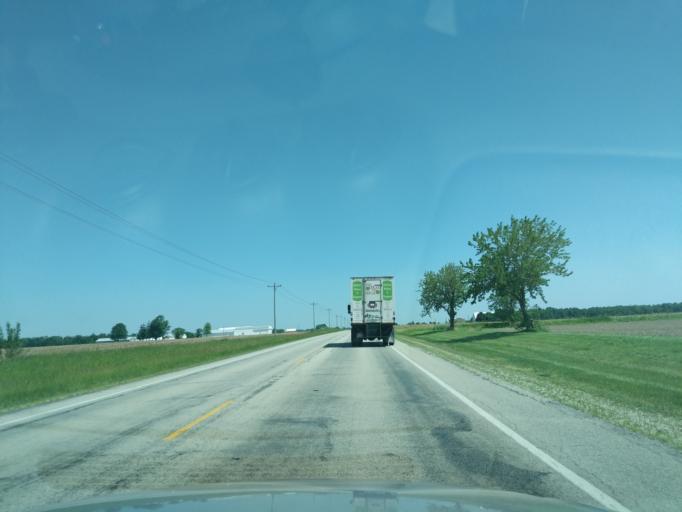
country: US
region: Indiana
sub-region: Huntington County
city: Roanoke
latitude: 41.0296
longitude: -85.4707
